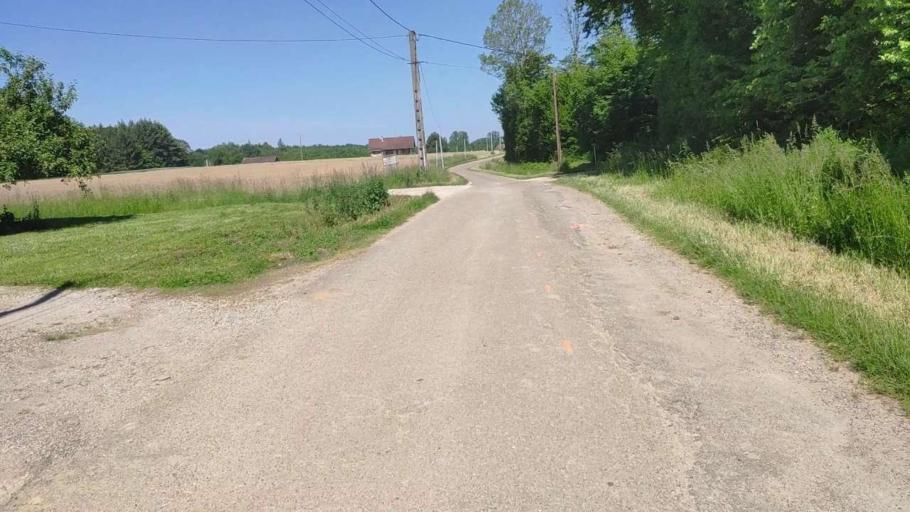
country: FR
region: Franche-Comte
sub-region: Departement du Jura
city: Bletterans
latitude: 46.7895
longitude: 5.4390
